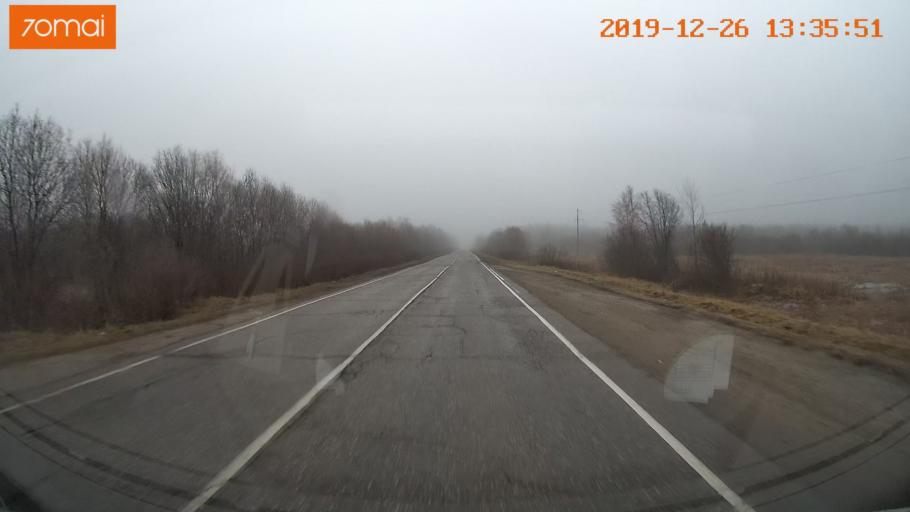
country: RU
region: Vologda
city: Sheksna
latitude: 58.7887
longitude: 38.3467
